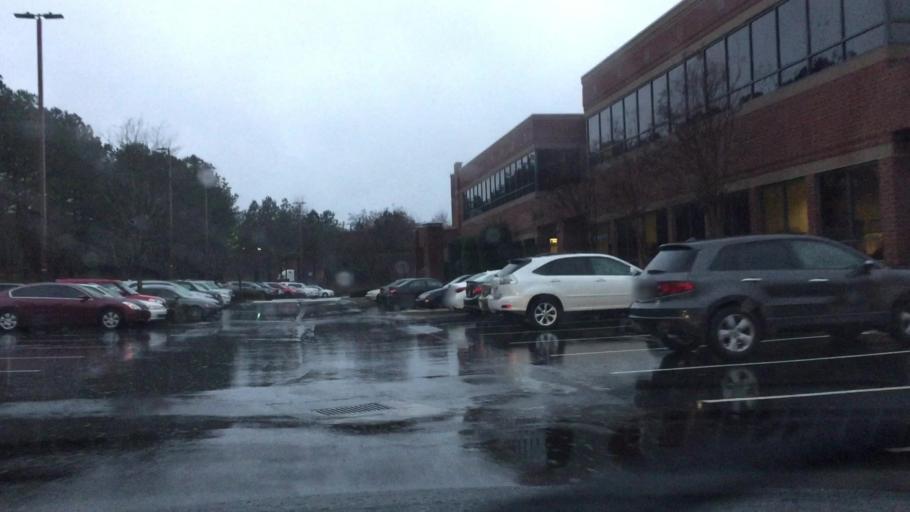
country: US
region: Georgia
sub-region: Cobb County
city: Marietta
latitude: 33.9812
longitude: -84.5204
